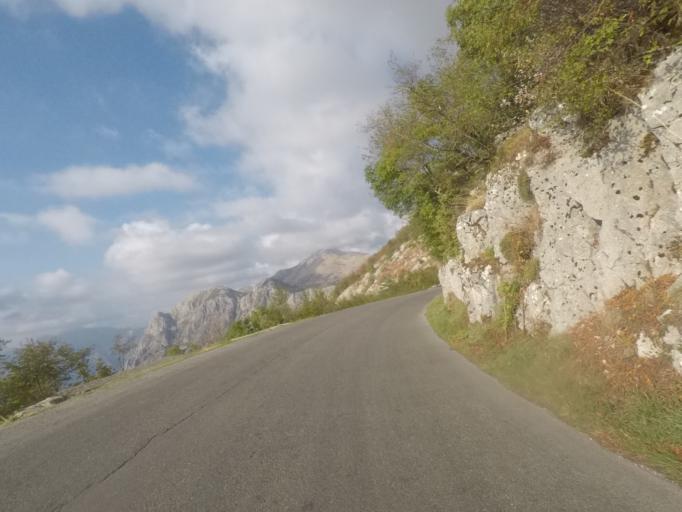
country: ME
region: Kotor
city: Kotor
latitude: 42.4103
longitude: 18.7896
